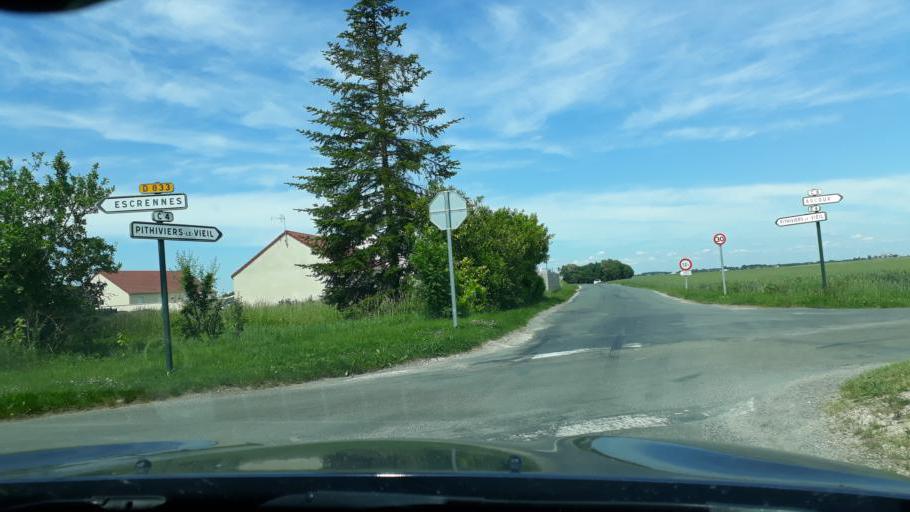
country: FR
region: Centre
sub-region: Departement du Loiret
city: Pithiviers-le-Vieil
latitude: 48.1204
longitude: 2.2218
